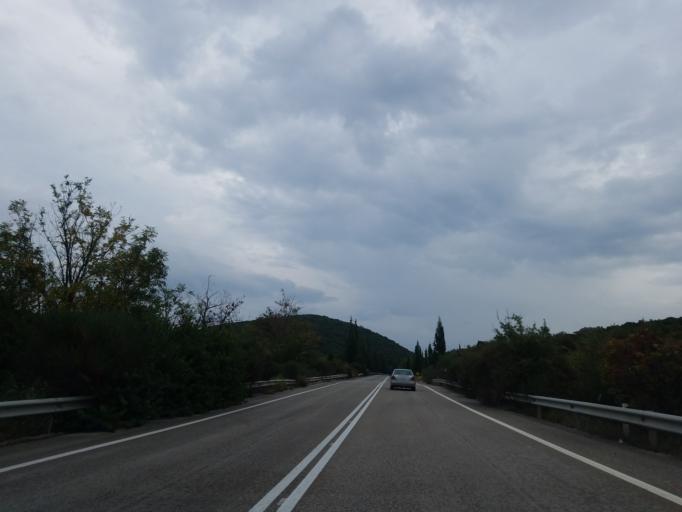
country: GR
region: Central Greece
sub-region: Nomos Voiotias
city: Livadeia
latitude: 38.4442
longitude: 22.8022
